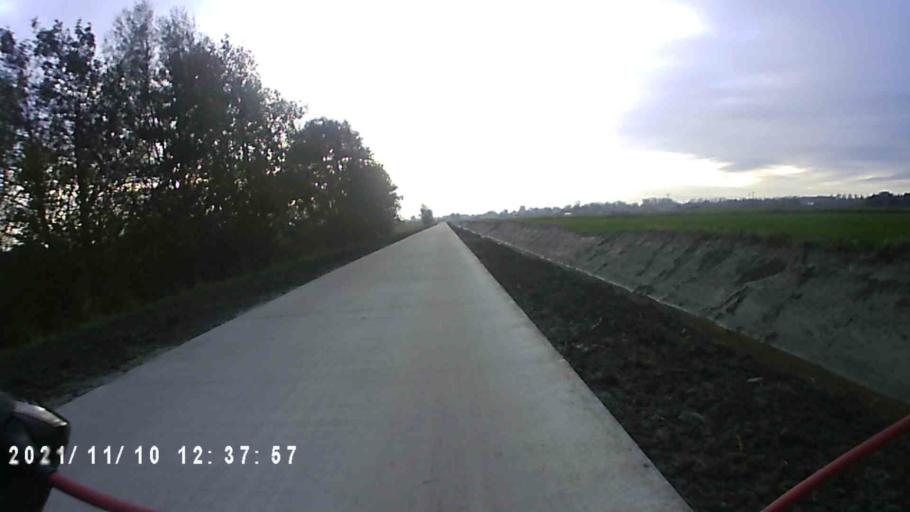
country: NL
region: Groningen
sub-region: Gemeente Groningen
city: Korrewegwijk
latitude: 53.2583
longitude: 6.5490
